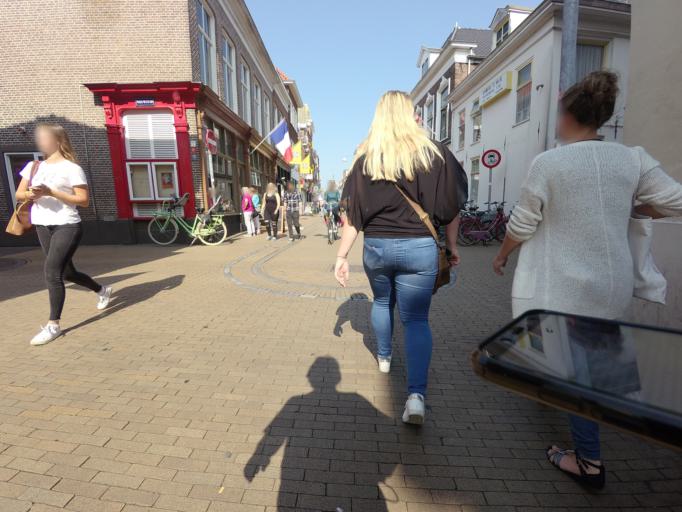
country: NL
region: Groningen
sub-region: Gemeente Groningen
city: Groningen
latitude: 53.2150
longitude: 6.5652
